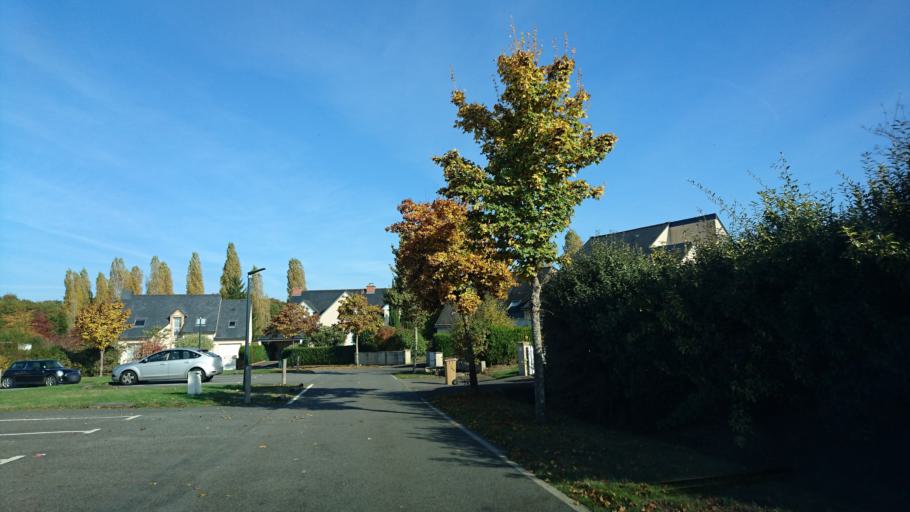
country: FR
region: Brittany
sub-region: Departement d'Ille-et-Vilaine
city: Bruz
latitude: 48.0396
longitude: -1.7599
